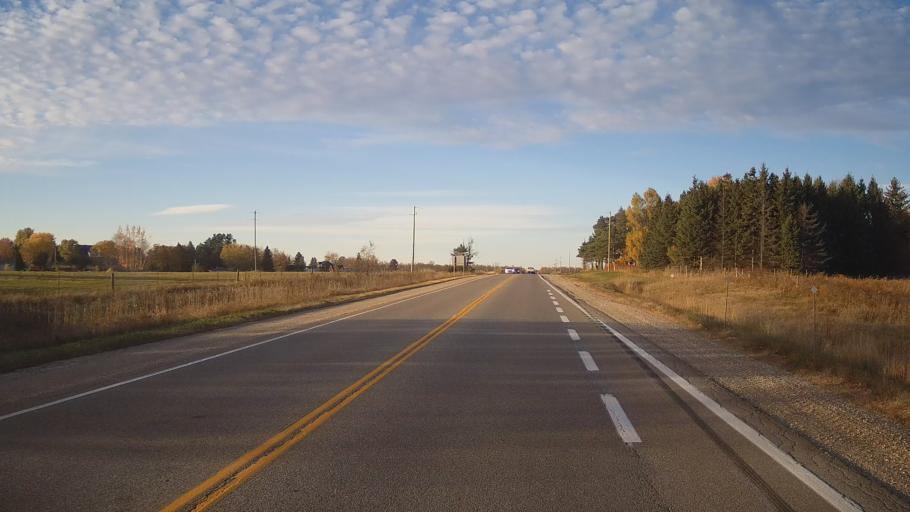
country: CA
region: Ontario
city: Perth
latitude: 44.9921
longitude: -76.2281
